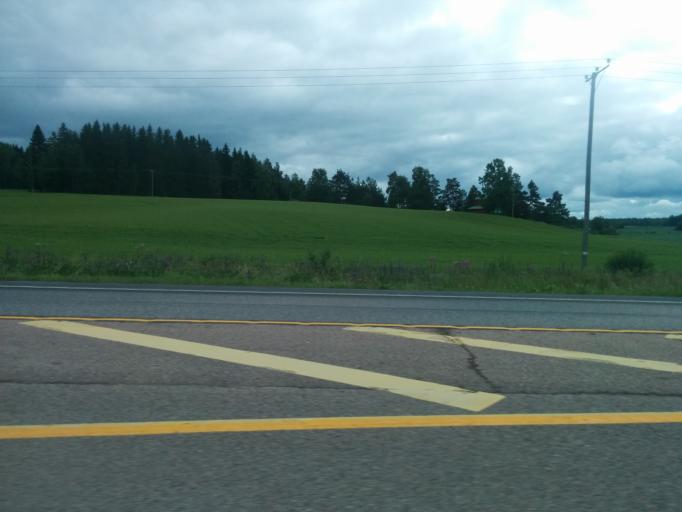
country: FI
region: Pirkanmaa
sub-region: Tampere
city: Orivesi
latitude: 61.6876
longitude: 24.3798
